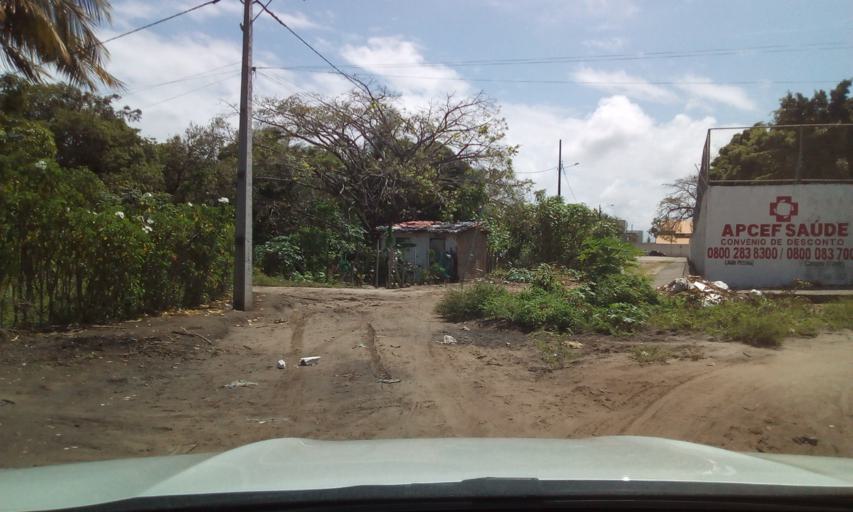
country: BR
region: Paraiba
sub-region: Joao Pessoa
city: Joao Pessoa
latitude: -7.1480
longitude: -34.8077
